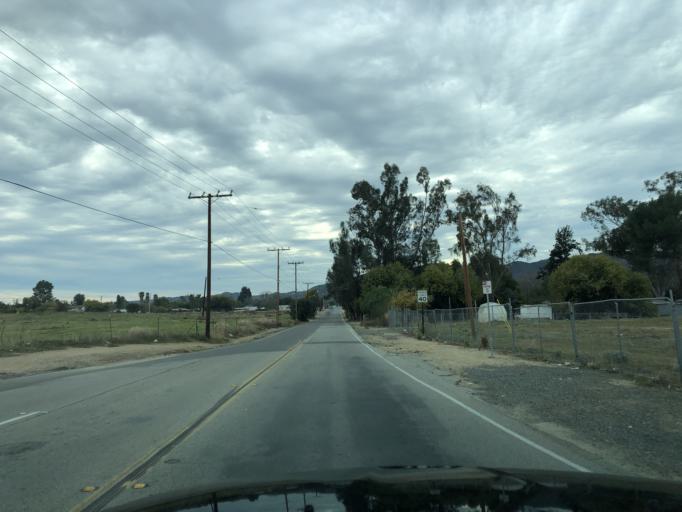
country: US
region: California
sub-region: Riverside County
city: Sedco Hills
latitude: 33.6266
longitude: -117.2754
